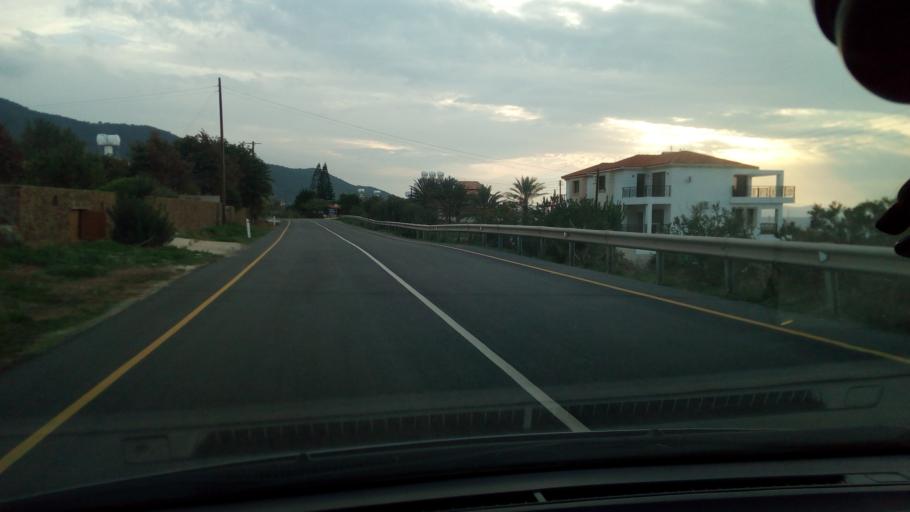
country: CY
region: Lefkosia
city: Kato Pyrgos
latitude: 35.1703
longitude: 32.5494
